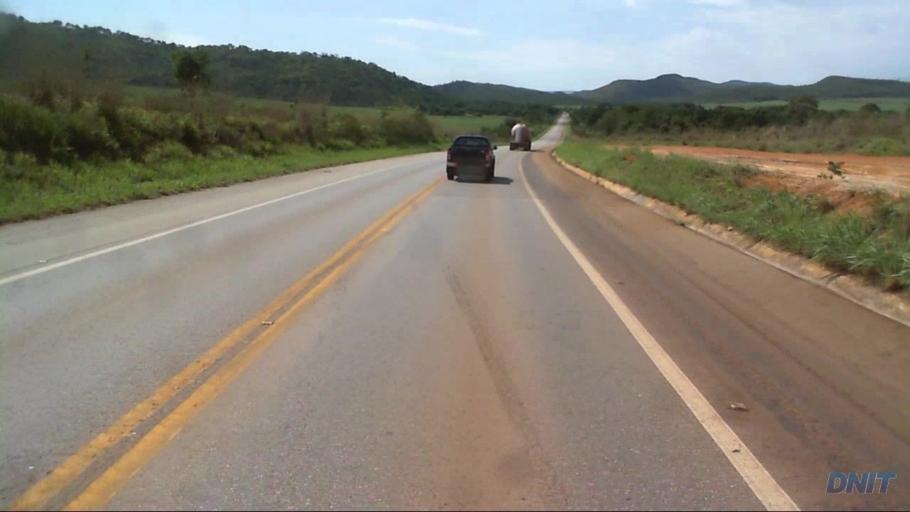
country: BR
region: Goias
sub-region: Barro Alto
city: Barro Alto
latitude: -15.1175
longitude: -48.8385
